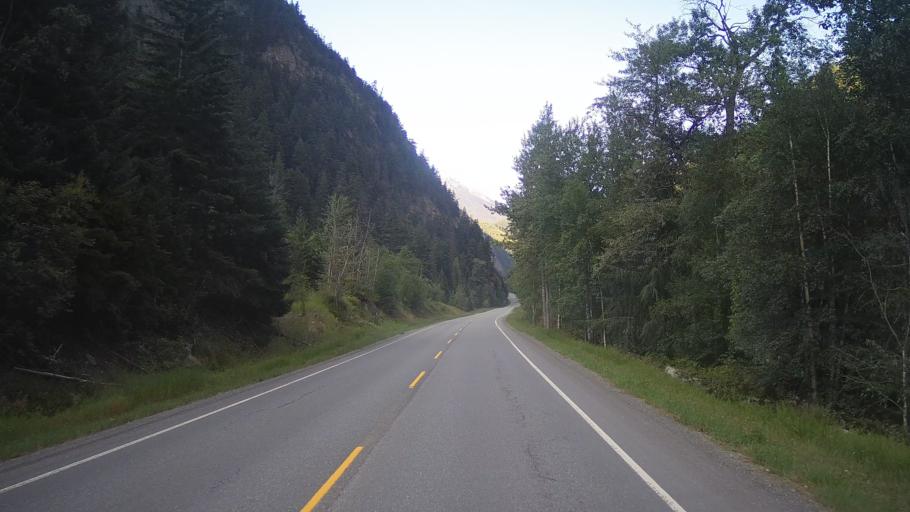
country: CA
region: British Columbia
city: Lillooet
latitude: 50.5551
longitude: -122.0975
